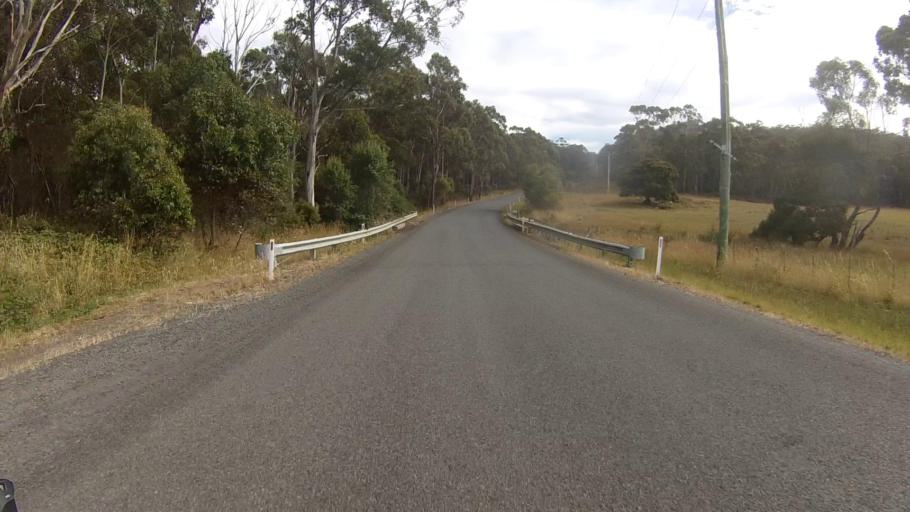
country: AU
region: Tasmania
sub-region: Sorell
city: Sorell
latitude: -42.8168
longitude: 147.7912
